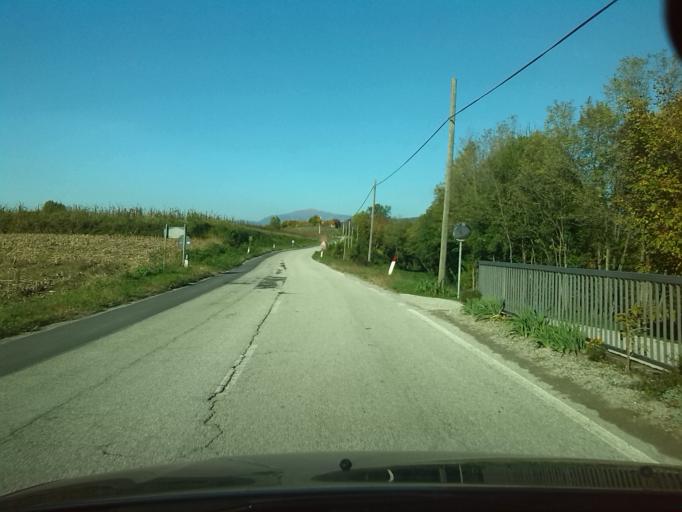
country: IT
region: Friuli Venezia Giulia
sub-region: Provincia di Gorizia
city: Dolegna del Collio
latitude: 46.0344
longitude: 13.4770
